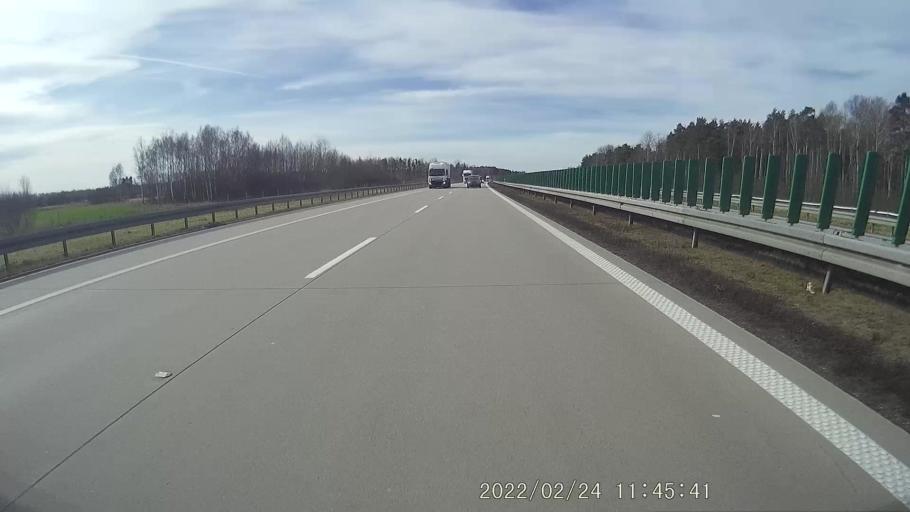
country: PL
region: Lower Silesian Voivodeship
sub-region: Powiat polkowicki
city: Radwanice
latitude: 51.5639
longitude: 15.9373
